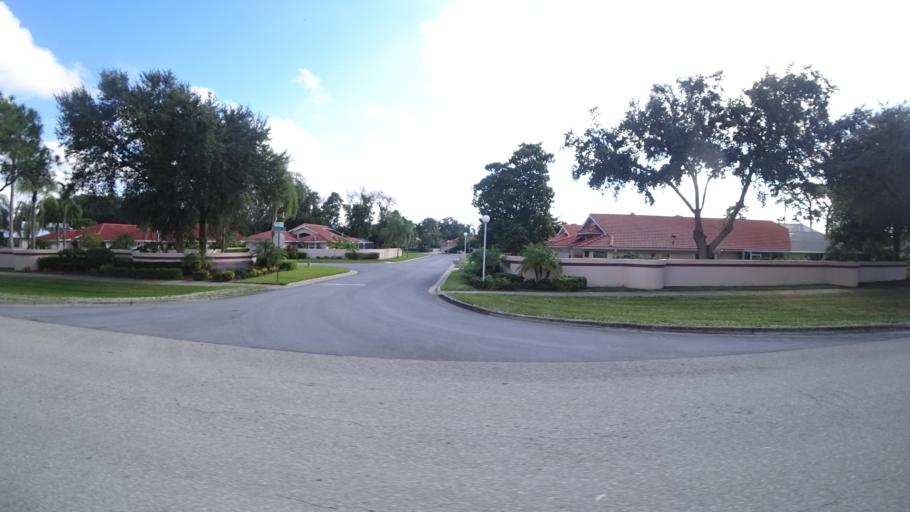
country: US
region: Florida
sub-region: Sarasota County
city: Desoto Lakes
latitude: 27.3959
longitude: -82.4871
